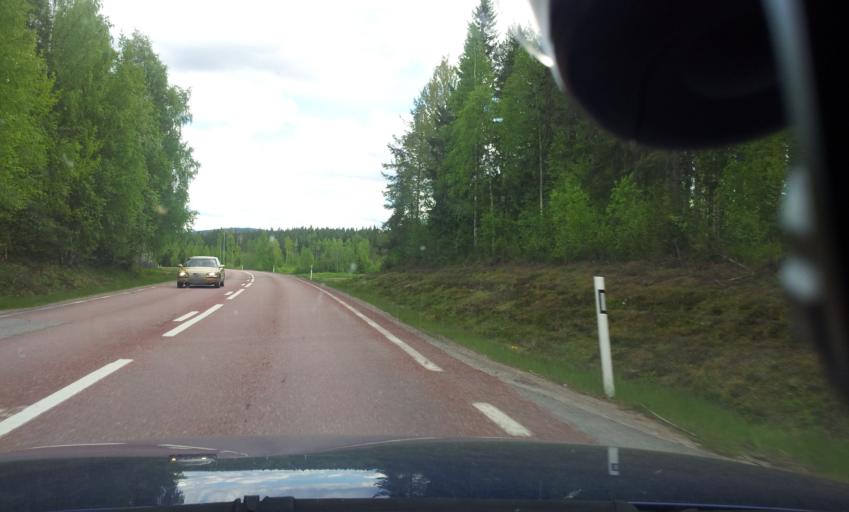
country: SE
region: Gaevleborg
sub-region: Ljusdals Kommun
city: Jaervsoe
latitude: 61.6567
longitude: 16.1605
